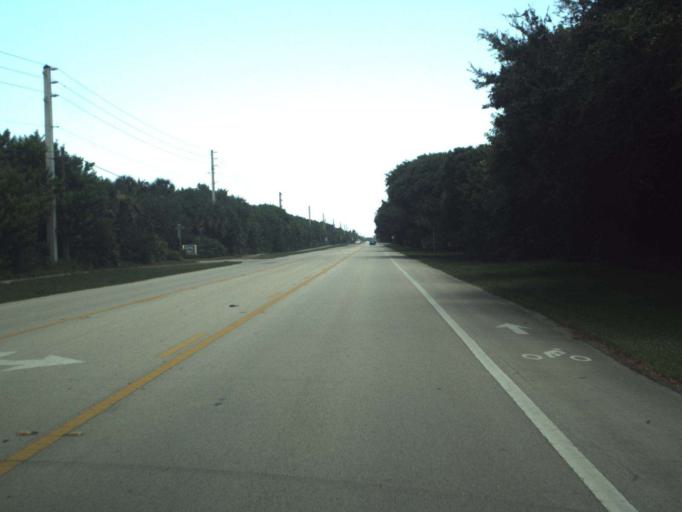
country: US
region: Florida
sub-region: Indian River County
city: Wabasso Beach
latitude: 27.7696
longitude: -80.4016
